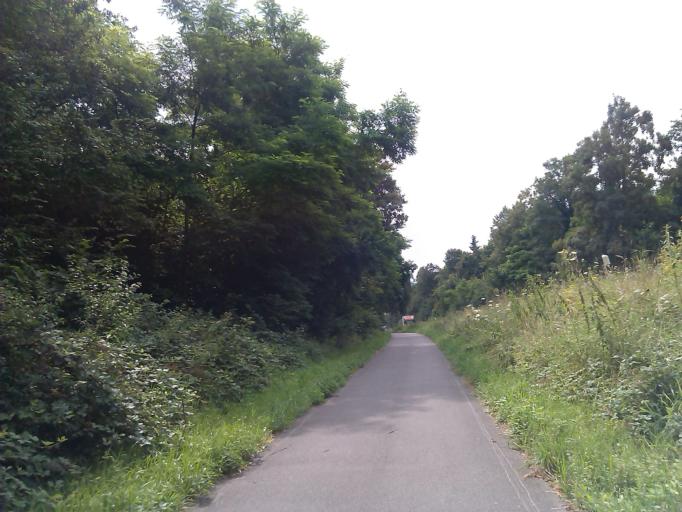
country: DE
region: Rheinland-Pfalz
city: Schifferstadt
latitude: 49.3578
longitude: 8.4038
